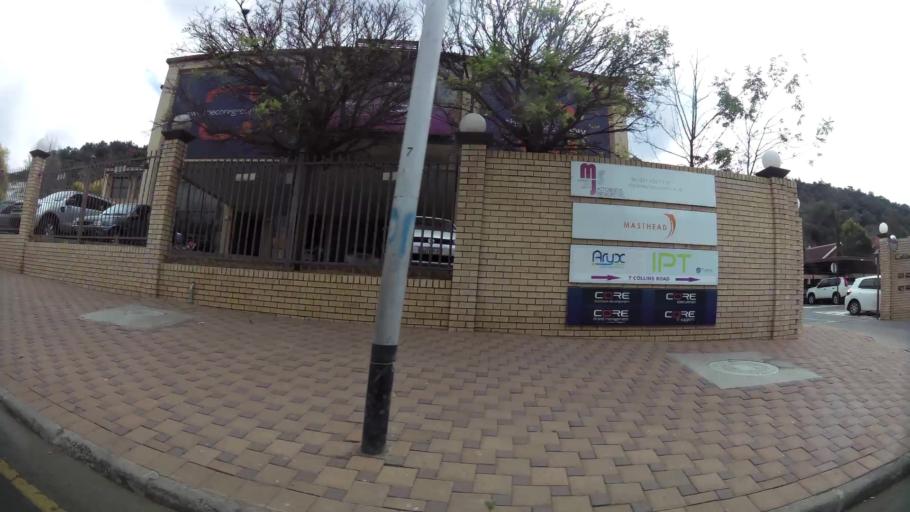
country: ZA
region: Orange Free State
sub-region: Mangaung Metropolitan Municipality
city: Bloemfontein
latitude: -29.1087
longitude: 26.2179
